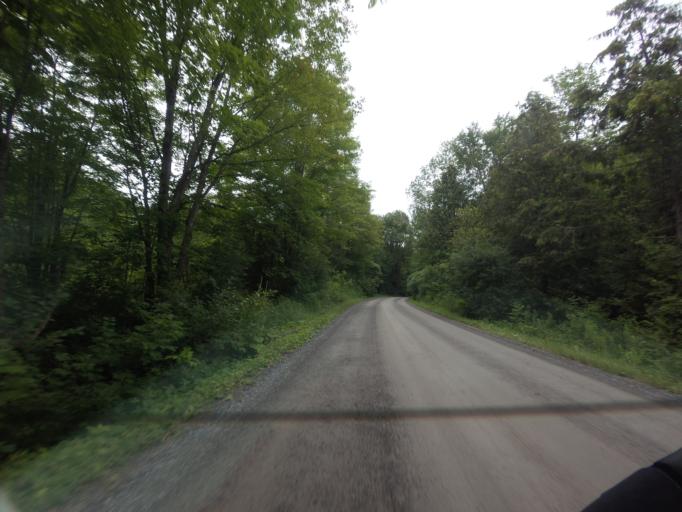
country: CA
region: Ontario
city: Kingston
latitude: 44.5982
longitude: -76.5279
